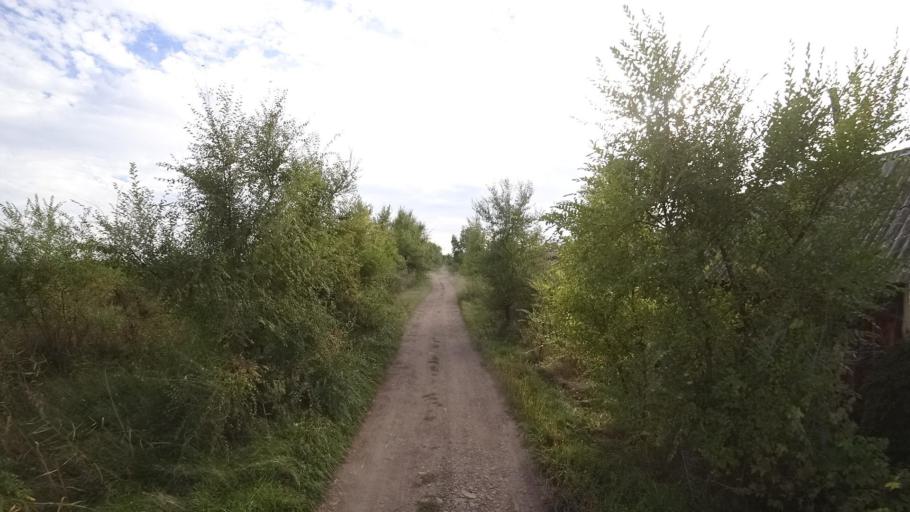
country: RU
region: Primorskiy
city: Dostoyevka
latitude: 44.2873
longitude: 133.4293
